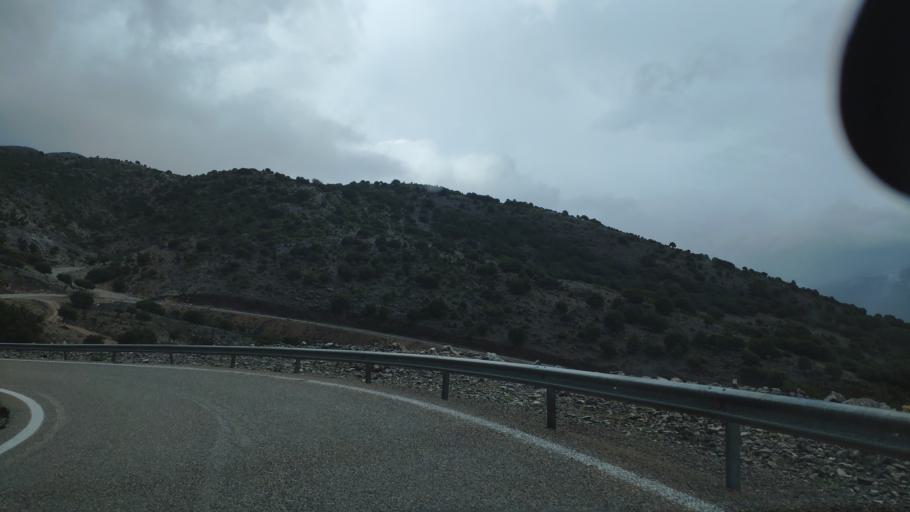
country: GR
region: Central Greece
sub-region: Nomos Evrytanias
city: Kerasochori
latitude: 39.0770
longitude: 21.3993
